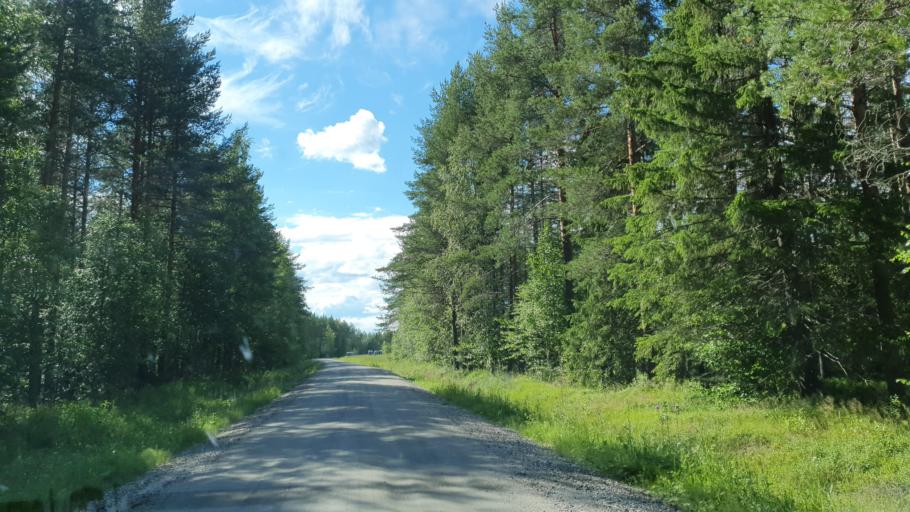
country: FI
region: Kainuu
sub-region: Kehys-Kainuu
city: Kuhmo
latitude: 64.1468
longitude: 29.7622
